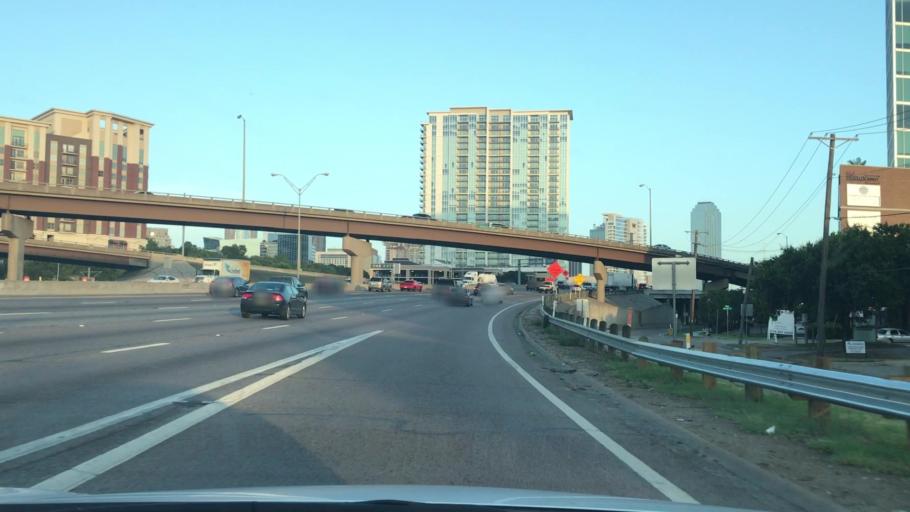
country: US
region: Texas
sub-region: Dallas County
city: Dallas
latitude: 32.7969
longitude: -96.8165
